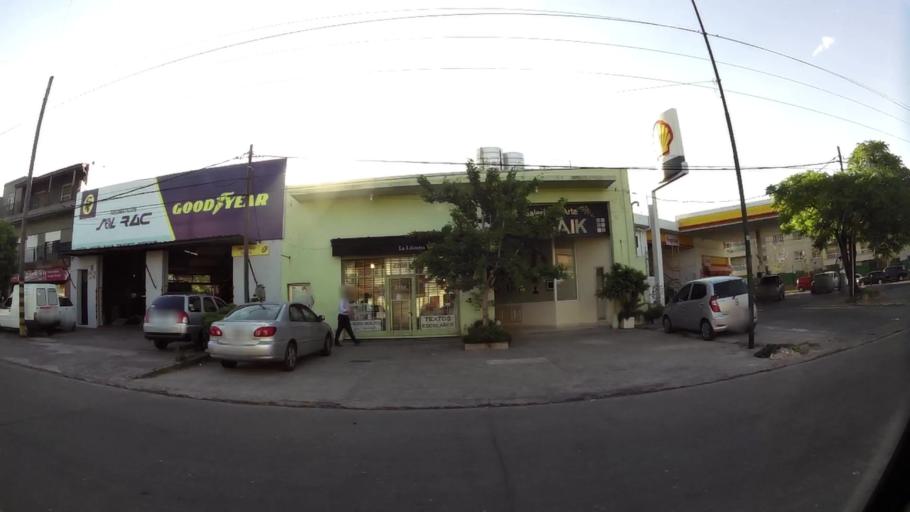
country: AR
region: Buenos Aires
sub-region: Partido de San Isidro
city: San Isidro
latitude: -34.4726
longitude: -58.5556
